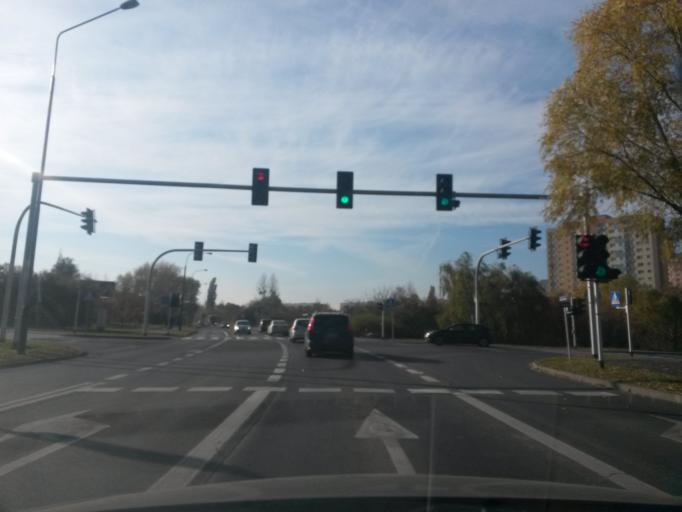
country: PL
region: Greater Poland Voivodeship
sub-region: Poznan
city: Poznan
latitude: 52.3812
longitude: 16.9573
